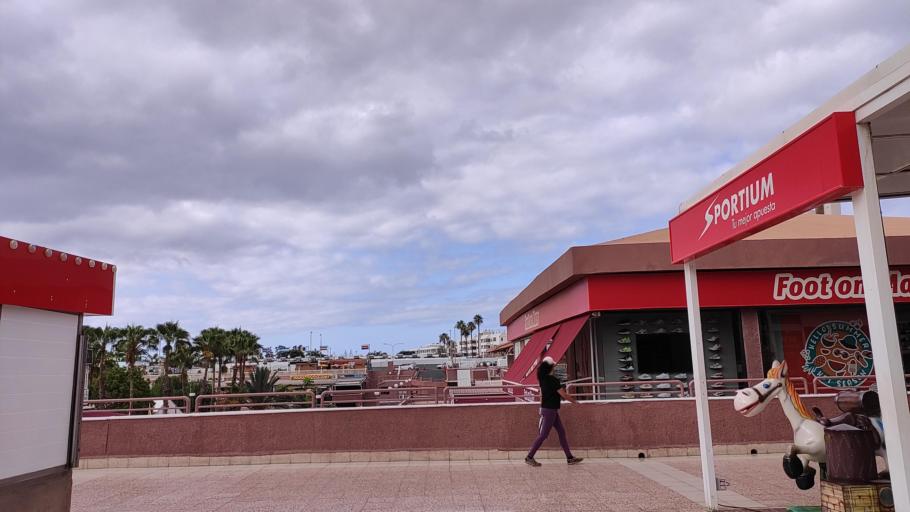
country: ES
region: Canary Islands
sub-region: Provincia de Las Palmas
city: Playa del Ingles
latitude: 27.7590
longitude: -15.5775
